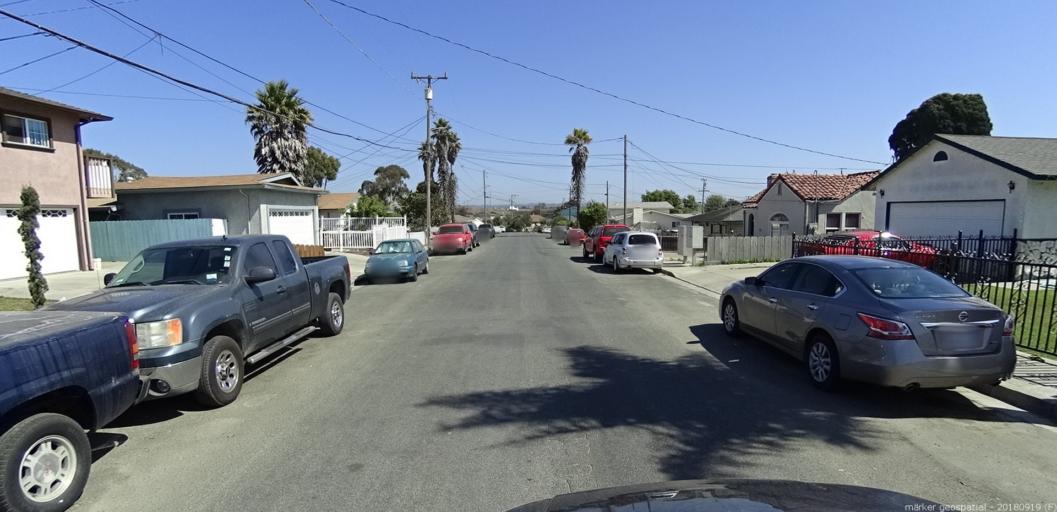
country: US
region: California
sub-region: Monterey County
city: Castroville
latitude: 36.7641
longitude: -121.7484
